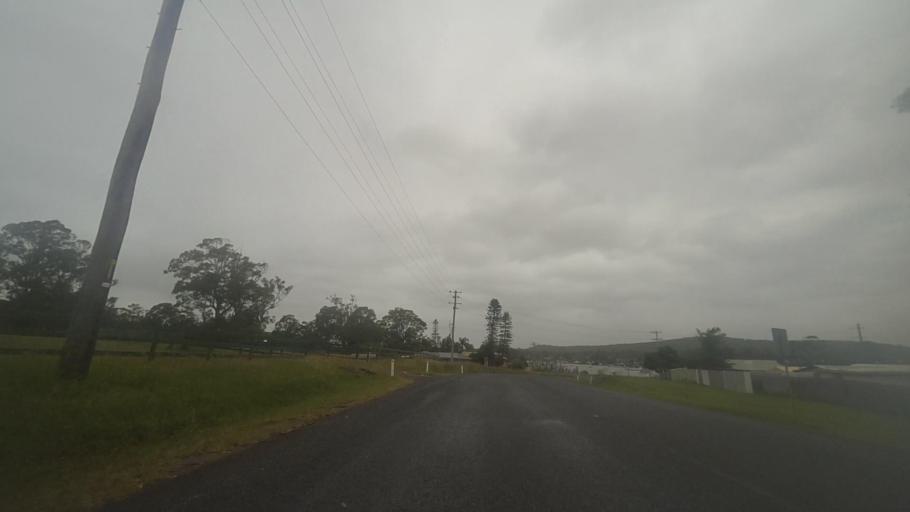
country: AU
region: New South Wales
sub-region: Port Stephens Shire
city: Port Stephens
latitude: -32.6524
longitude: 151.9717
